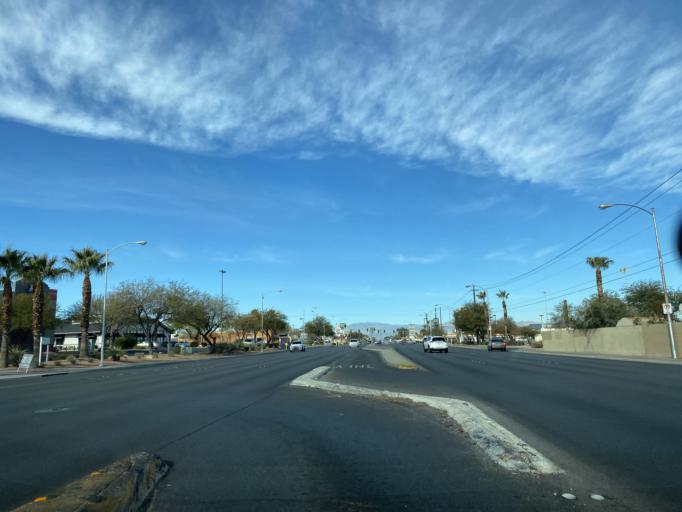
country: US
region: Nevada
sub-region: Clark County
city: Spring Valley
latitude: 36.1235
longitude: -115.2429
